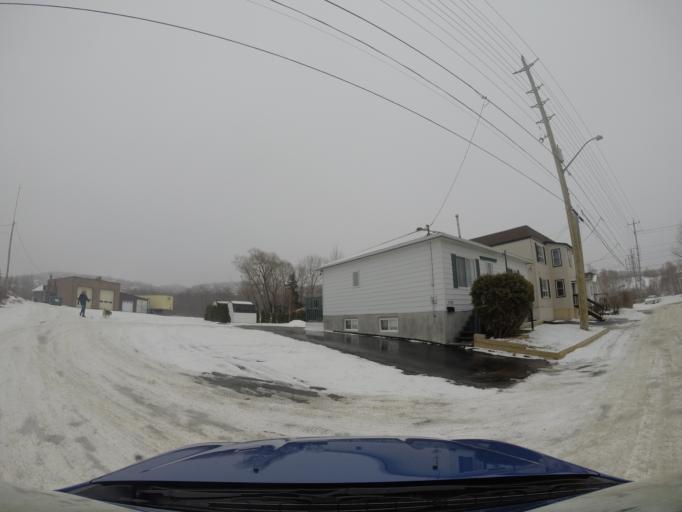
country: CA
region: Ontario
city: Greater Sudbury
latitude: 46.5049
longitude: -80.9805
